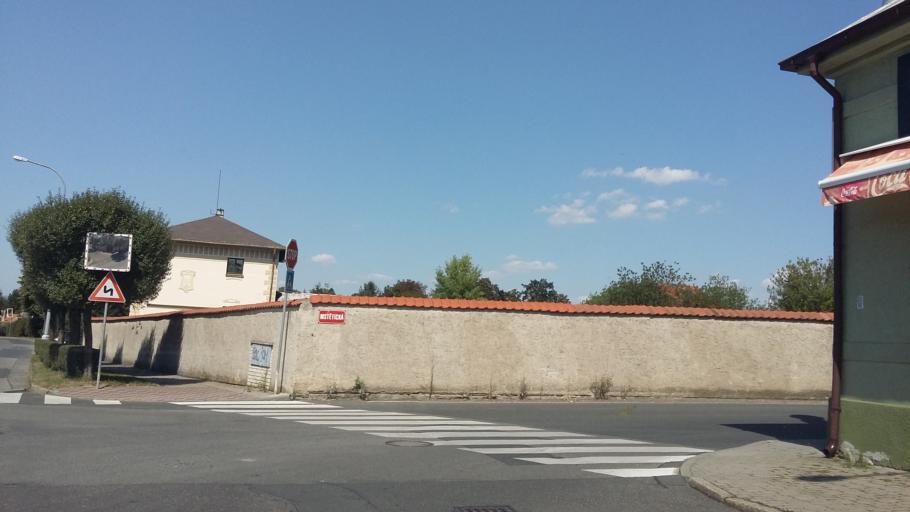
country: CZ
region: Central Bohemia
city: Zelenec
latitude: 50.1335
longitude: 14.6606
